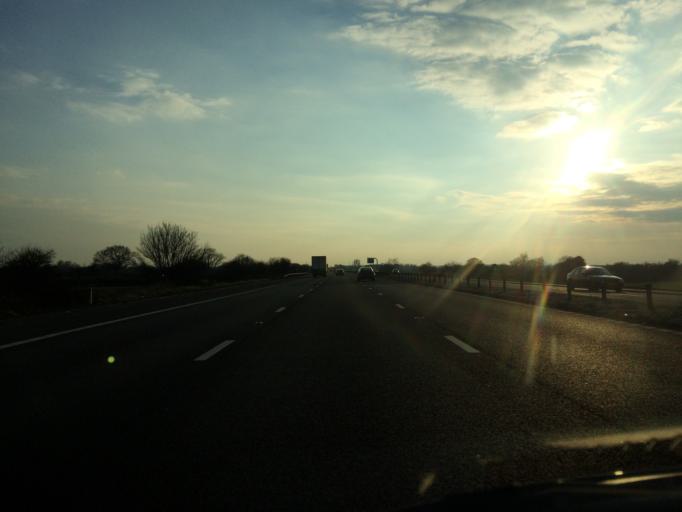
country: GB
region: England
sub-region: Wiltshire
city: Lyneham
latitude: 51.5304
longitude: -2.0220
